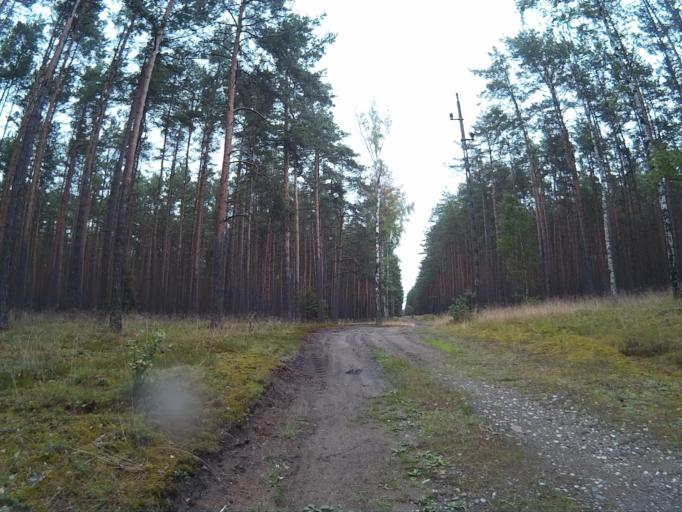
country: PL
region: Kujawsko-Pomorskie
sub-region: Powiat swiecki
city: Osie
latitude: 53.6123
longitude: 18.3947
